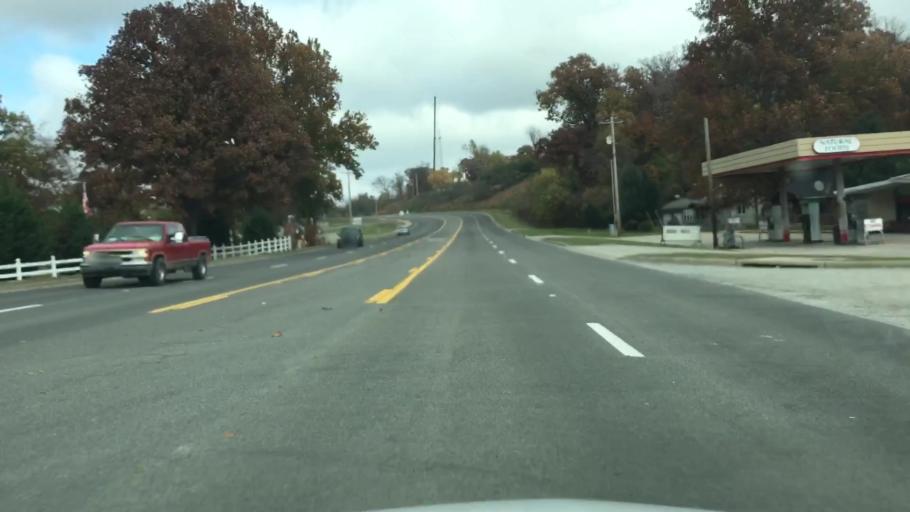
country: US
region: Arkansas
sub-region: Benton County
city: Gentry
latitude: 36.2461
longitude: -94.4863
